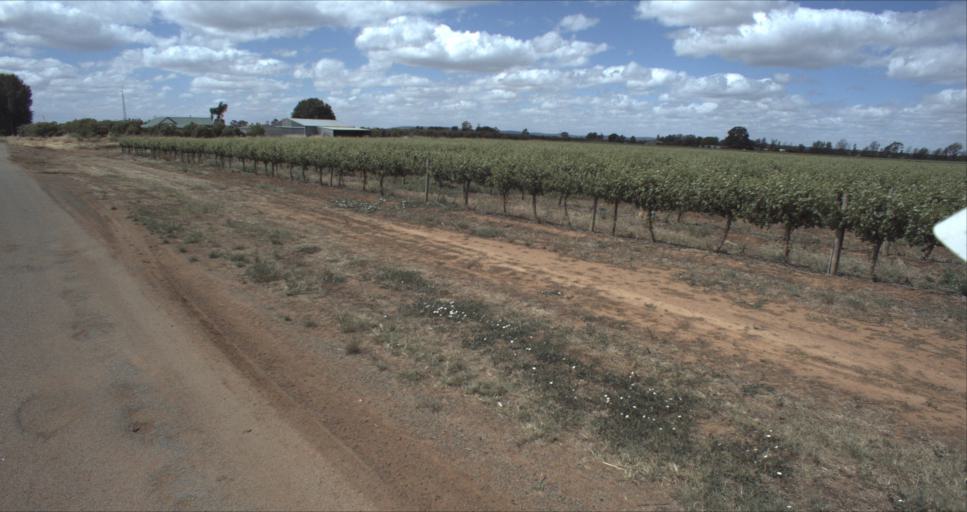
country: AU
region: New South Wales
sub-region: Leeton
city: Leeton
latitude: -34.5862
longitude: 146.3913
